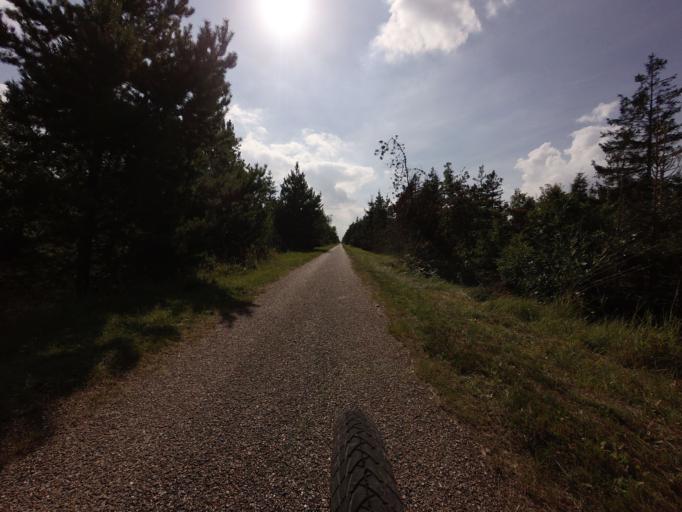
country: DK
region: Central Jutland
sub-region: Viborg Kommune
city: Karup
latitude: 56.2653
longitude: 9.1128
